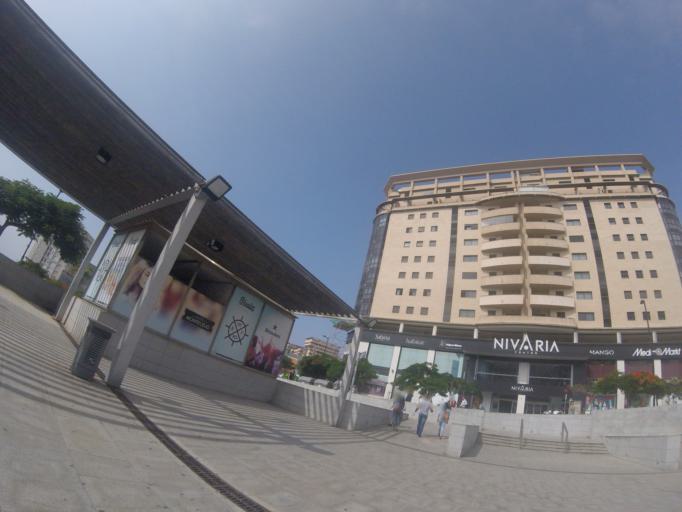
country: ES
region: Canary Islands
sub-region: Provincia de Santa Cruz de Tenerife
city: Santa Cruz de Tenerife
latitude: 28.4589
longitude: -16.2551
